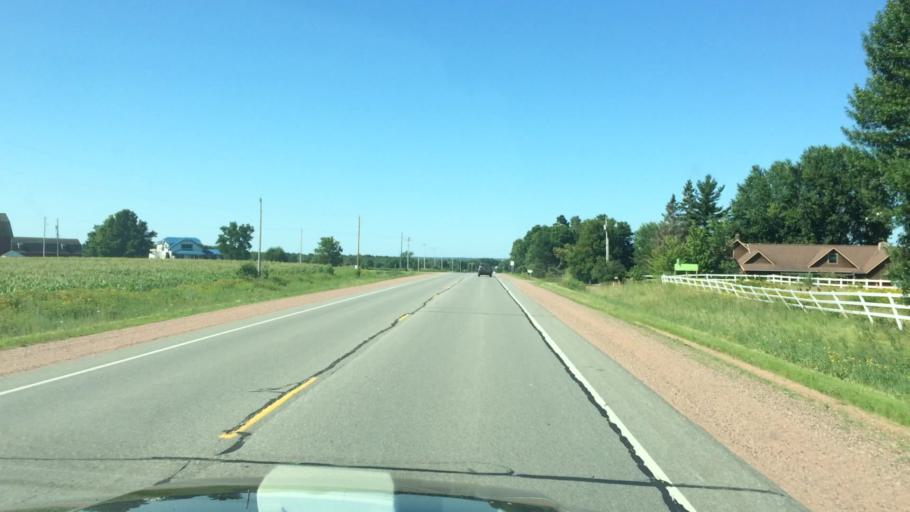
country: US
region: Wisconsin
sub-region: Marathon County
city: Stratford
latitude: 44.7301
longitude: -90.0872
